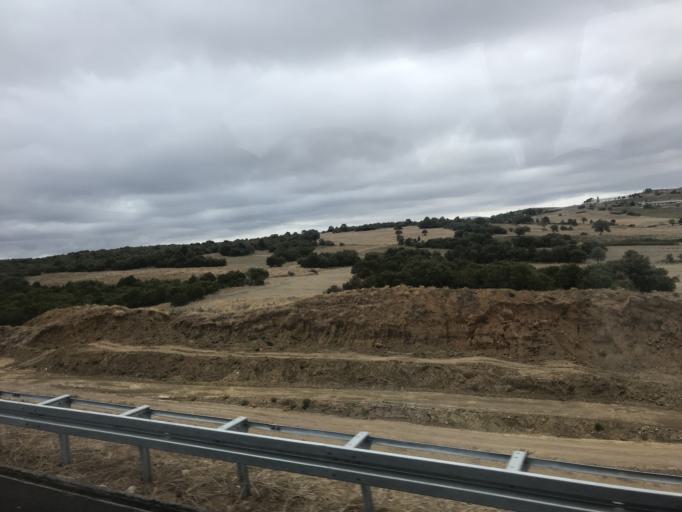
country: TR
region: Balikesir
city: Yenikoy
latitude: 39.7855
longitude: 28.0237
